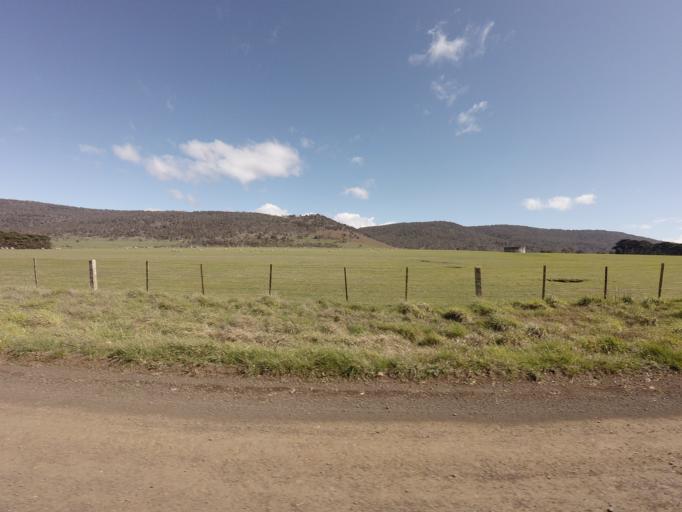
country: AU
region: Tasmania
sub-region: Northern Midlands
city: Evandale
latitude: -41.9525
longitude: 147.4355
